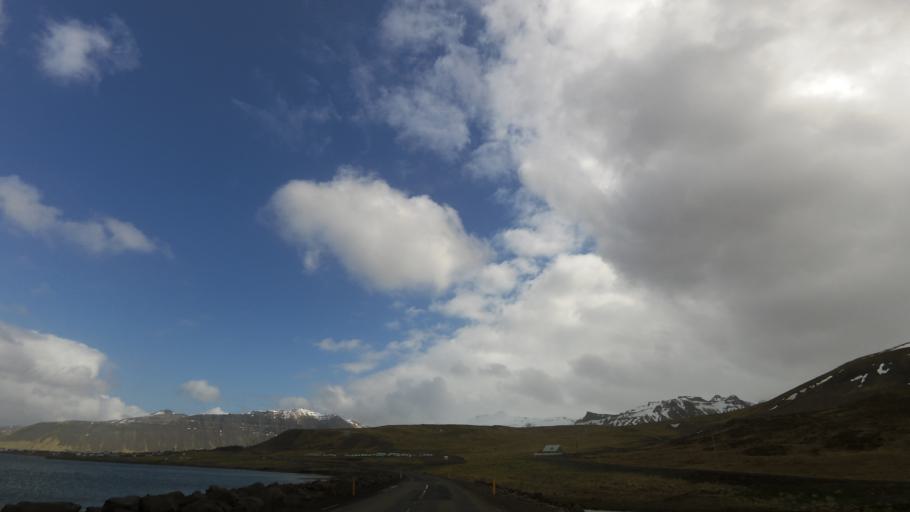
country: IS
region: West
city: Olafsvik
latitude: 64.9228
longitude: -23.2949
